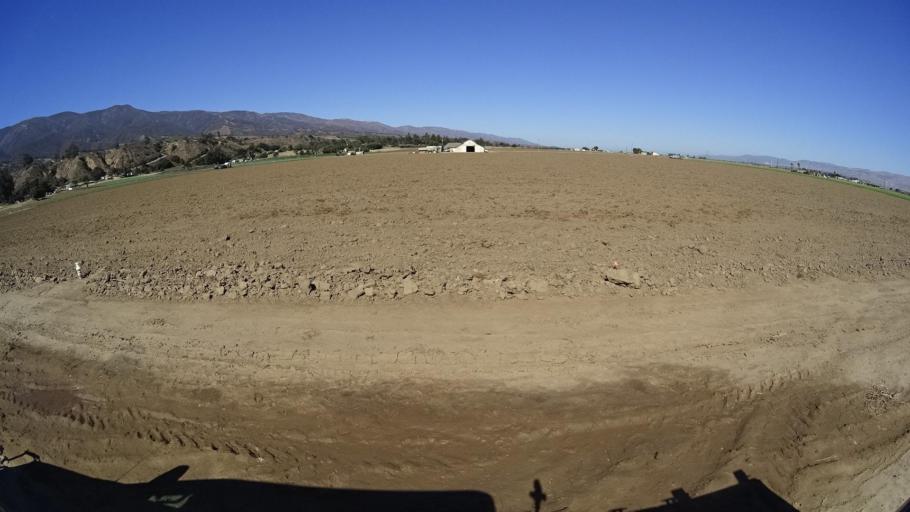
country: US
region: California
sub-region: Monterey County
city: Soledad
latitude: 36.3863
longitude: -121.3503
